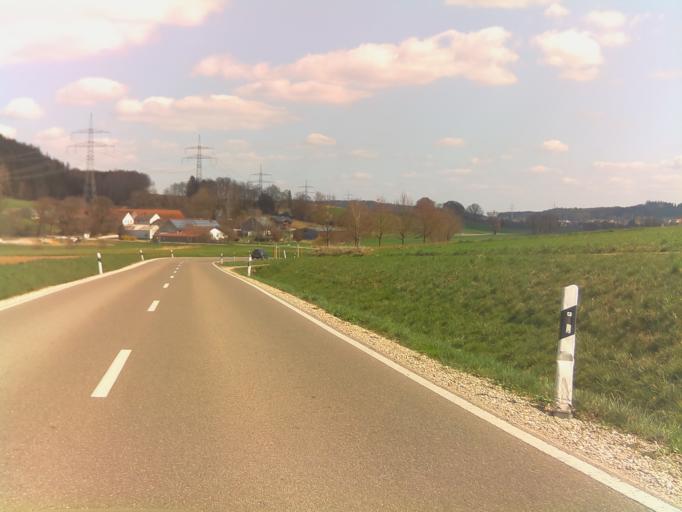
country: DE
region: Bavaria
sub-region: Swabia
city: Aindling
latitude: 48.5119
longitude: 10.9832
